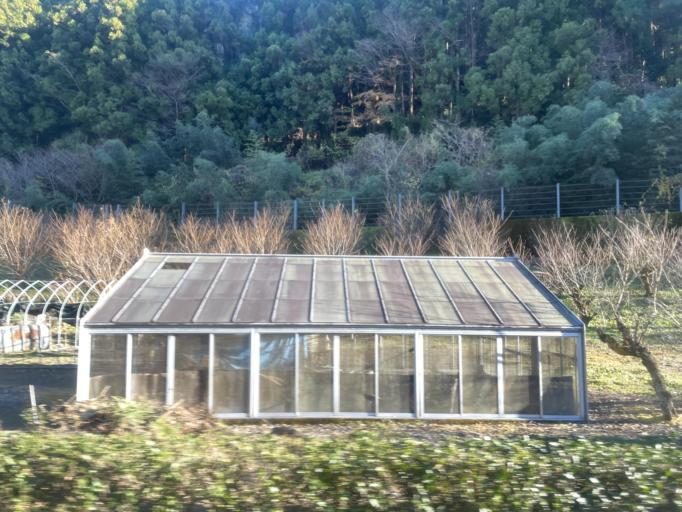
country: JP
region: Saitama
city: Yorii
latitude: 36.0608
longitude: 139.1794
